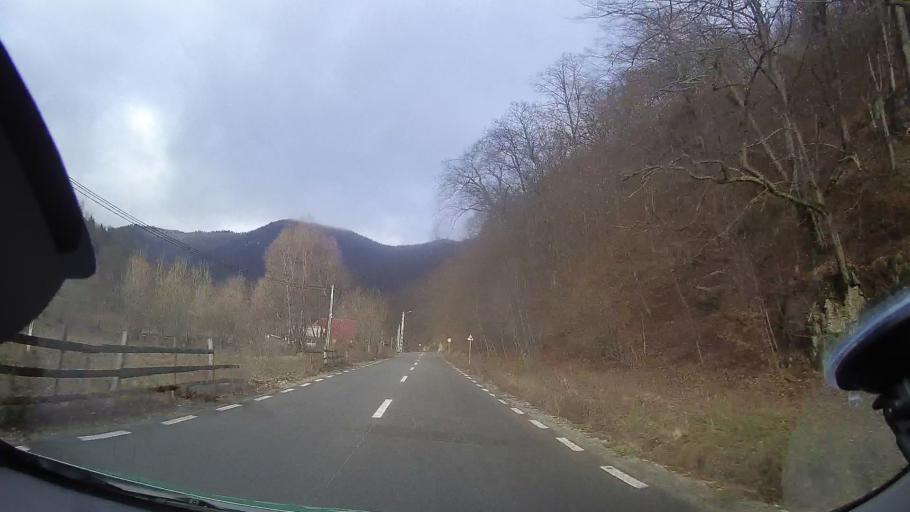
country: RO
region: Cluj
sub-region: Comuna Valea Ierii
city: Valea Ierii
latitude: 46.6435
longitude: 23.3522
